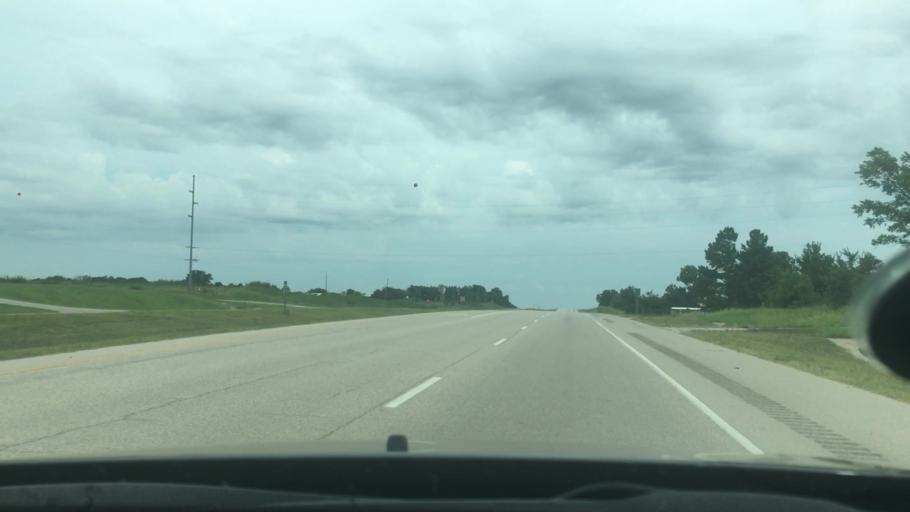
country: US
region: Oklahoma
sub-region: Pontotoc County
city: Byng
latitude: 34.9110
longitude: -96.6788
